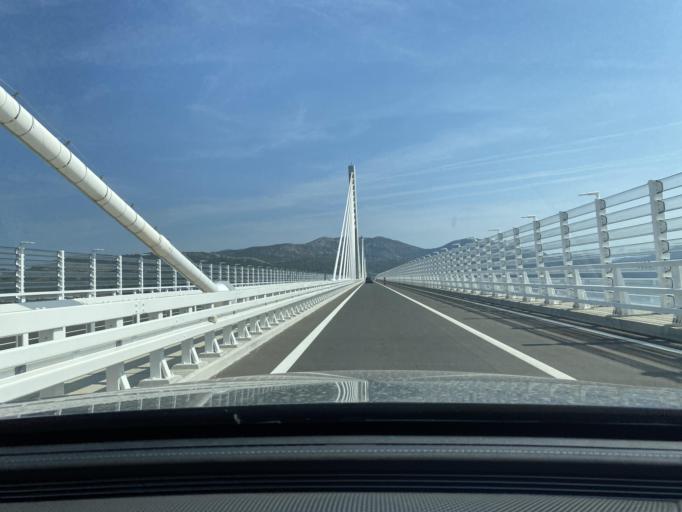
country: BA
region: Federation of Bosnia and Herzegovina
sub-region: Hercegovacko-Bosanski Kanton
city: Neum
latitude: 42.9273
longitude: 17.5317
